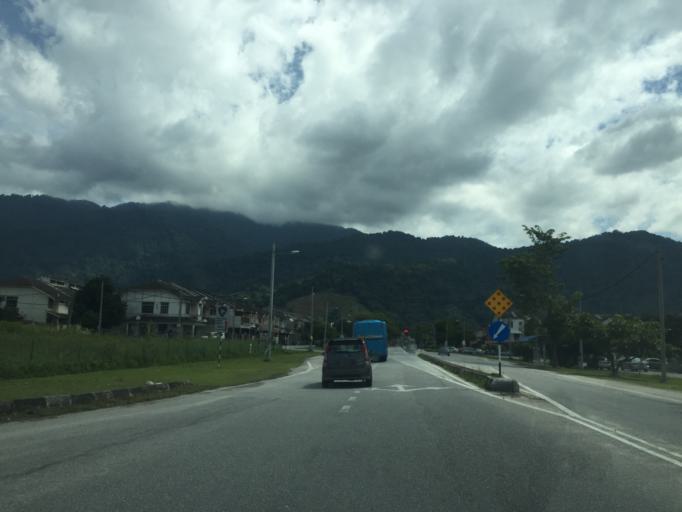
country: MY
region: Perak
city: Kampar
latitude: 4.3254
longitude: 101.1473
